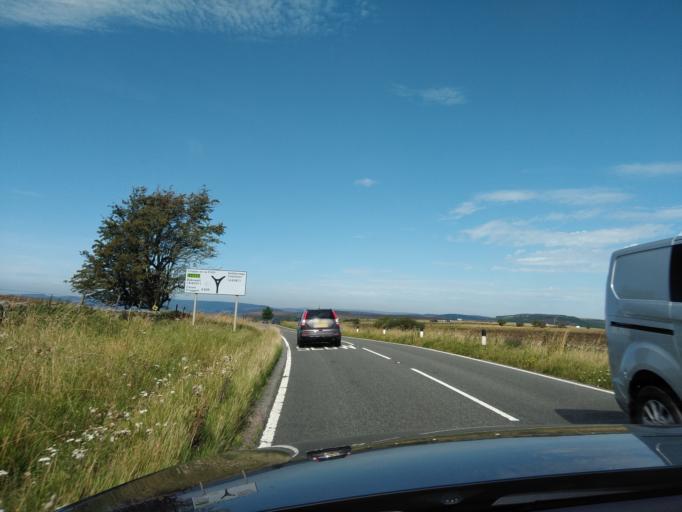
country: GB
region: England
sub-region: Derbyshire
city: Hathersage
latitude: 53.3057
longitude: -1.5957
